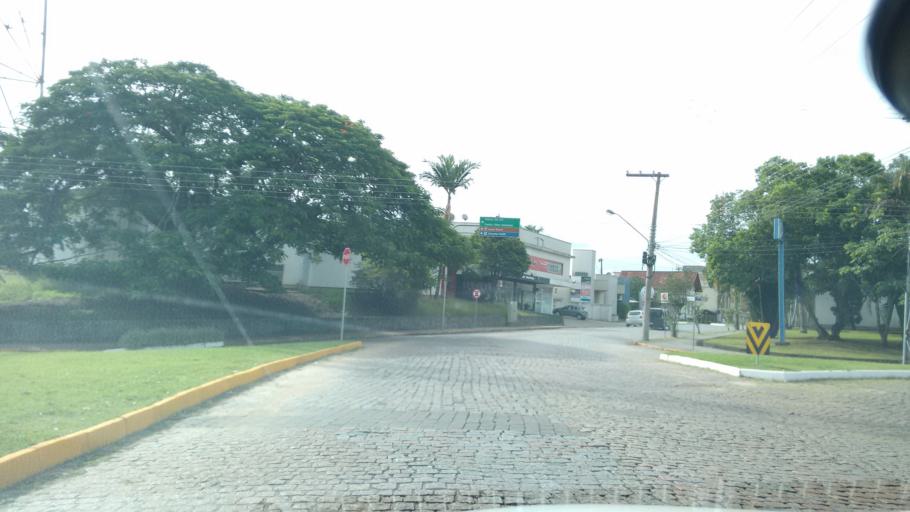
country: BR
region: Santa Catarina
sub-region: Timbo
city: Timbo
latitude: -26.8256
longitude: -49.2712
